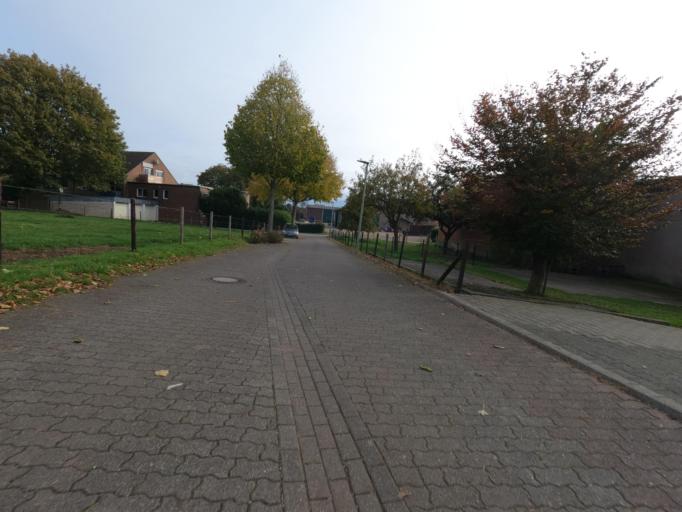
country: DE
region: North Rhine-Westphalia
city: Erkelenz
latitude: 51.0304
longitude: 6.3134
